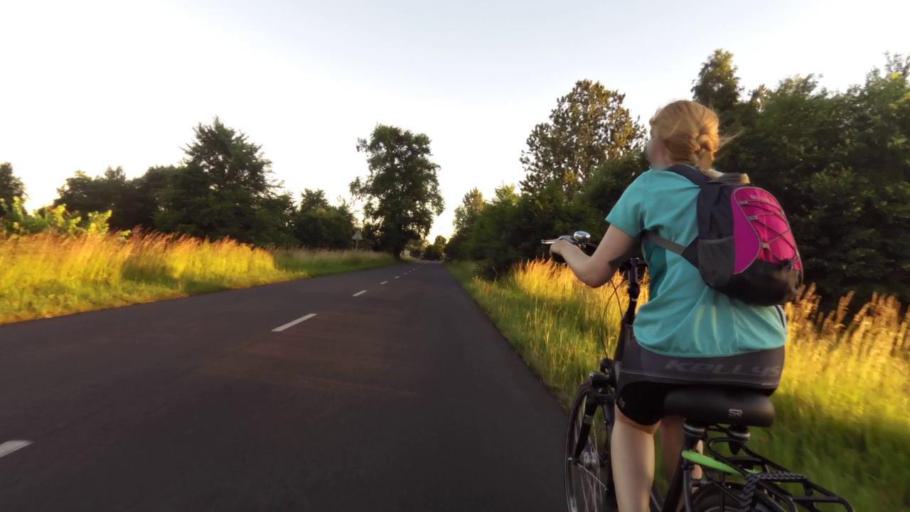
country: PL
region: West Pomeranian Voivodeship
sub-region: Powiat bialogardzki
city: Bialogard
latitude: 54.0157
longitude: 16.0082
